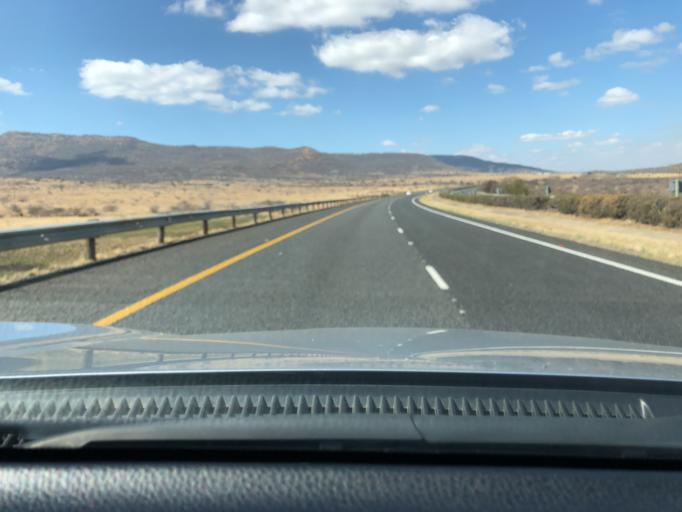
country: ZA
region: KwaZulu-Natal
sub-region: uThukela District Municipality
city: Ladysmith
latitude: -28.6912
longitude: 29.6365
